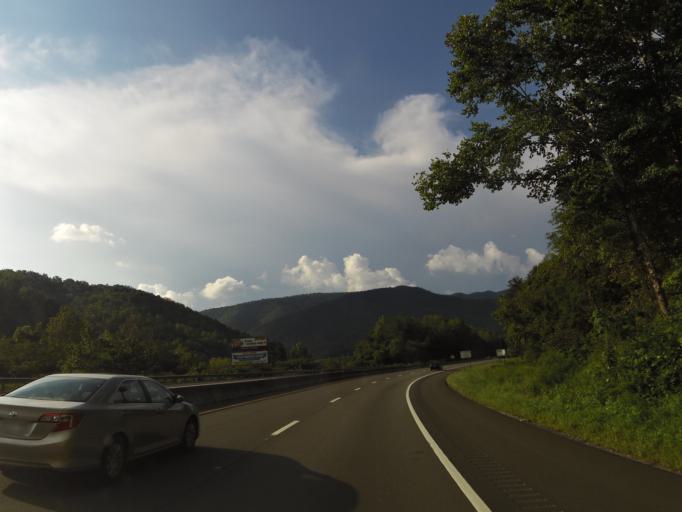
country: US
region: Tennessee
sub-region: Cocke County
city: Newport
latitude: 35.8101
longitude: -83.1424
